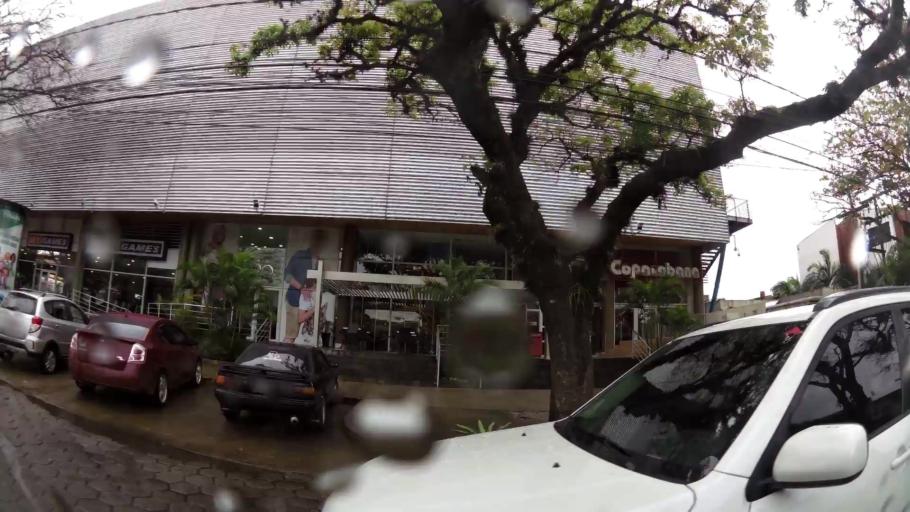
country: BO
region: Santa Cruz
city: Santa Cruz de la Sierra
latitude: -17.7979
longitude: -63.1787
